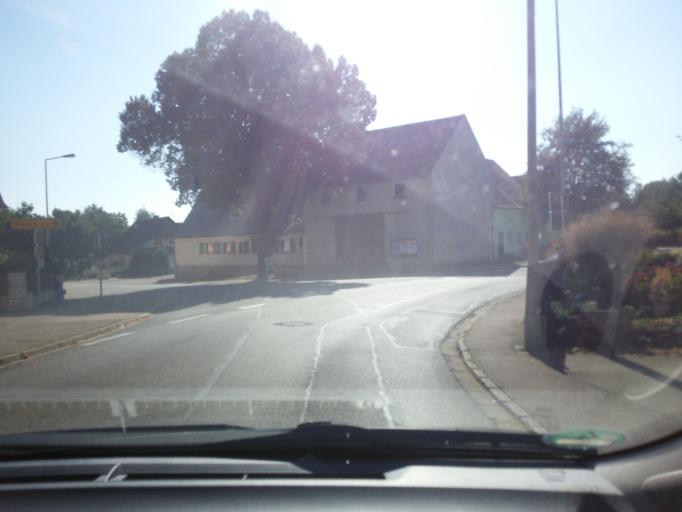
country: DE
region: Bavaria
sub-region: Swabia
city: Hainsfarth
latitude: 48.9824
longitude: 10.6103
